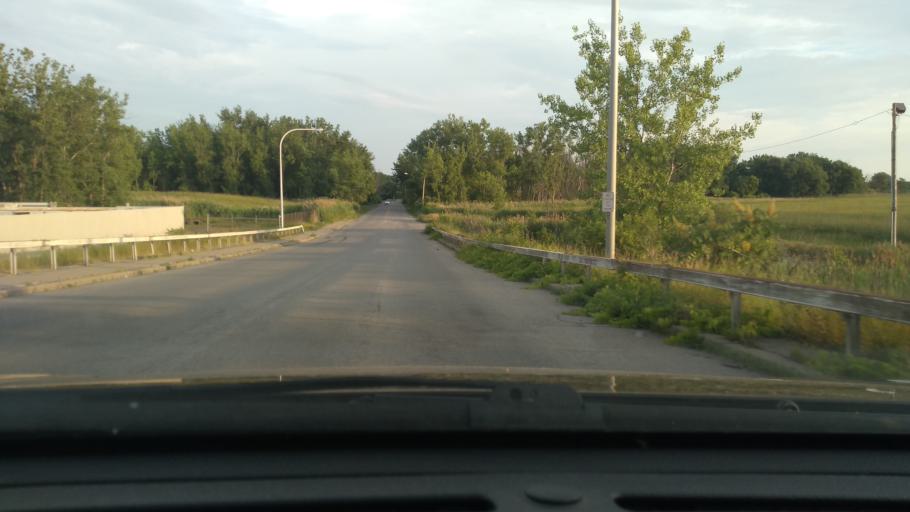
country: US
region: New York
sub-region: Erie County
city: Lackawanna
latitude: 42.8356
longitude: -78.8325
